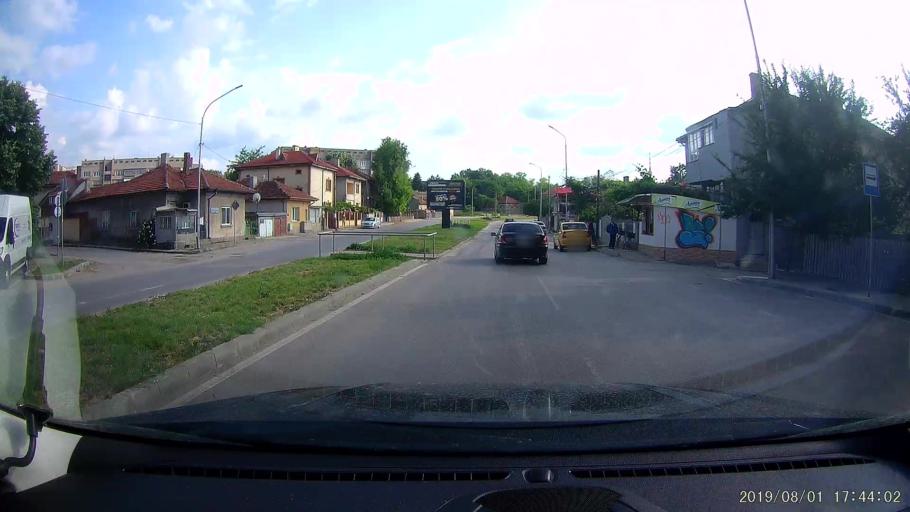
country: BG
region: Silistra
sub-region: Obshtina Silistra
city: Silistra
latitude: 44.1117
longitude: 27.2720
